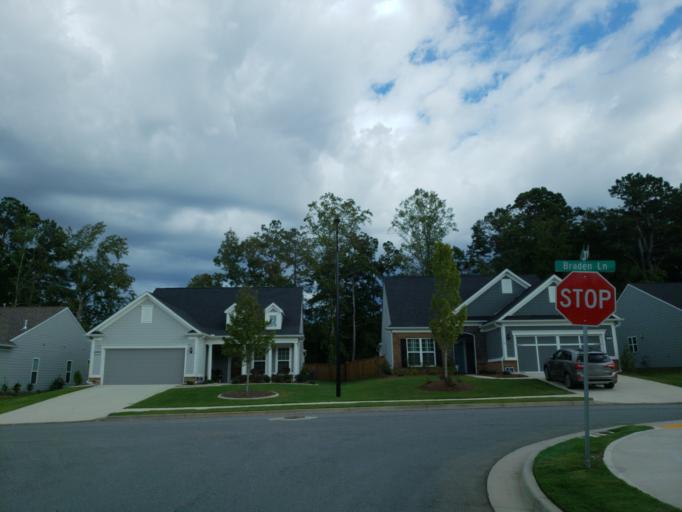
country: US
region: Georgia
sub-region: Cobb County
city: Kennesaw
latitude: 34.0566
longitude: -84.5778
